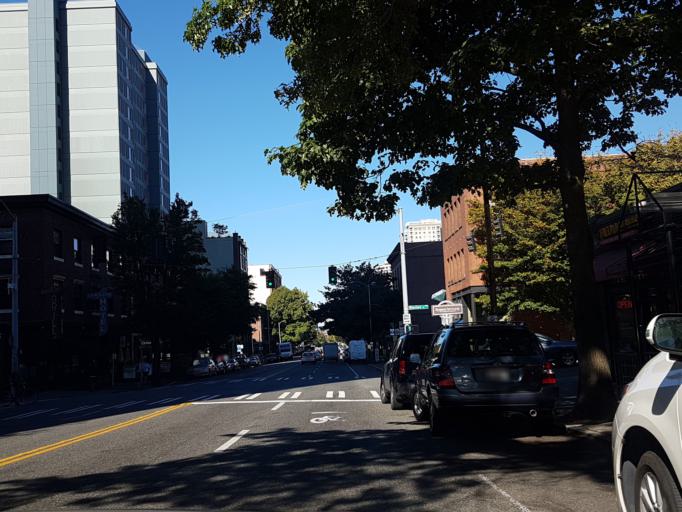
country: US
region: Washington
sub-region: King County
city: Seattle
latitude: 47.6124
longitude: -122.3448
